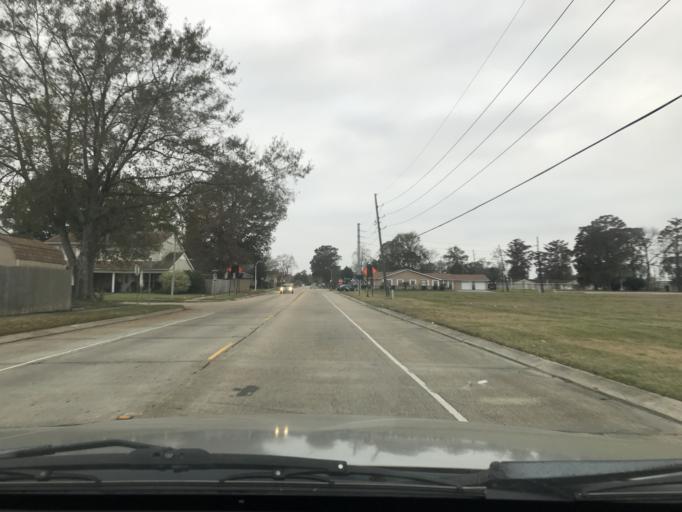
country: US
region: Louisiana
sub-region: Jefferson Parish
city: Woodmere
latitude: 29.8676
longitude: -90.0800
